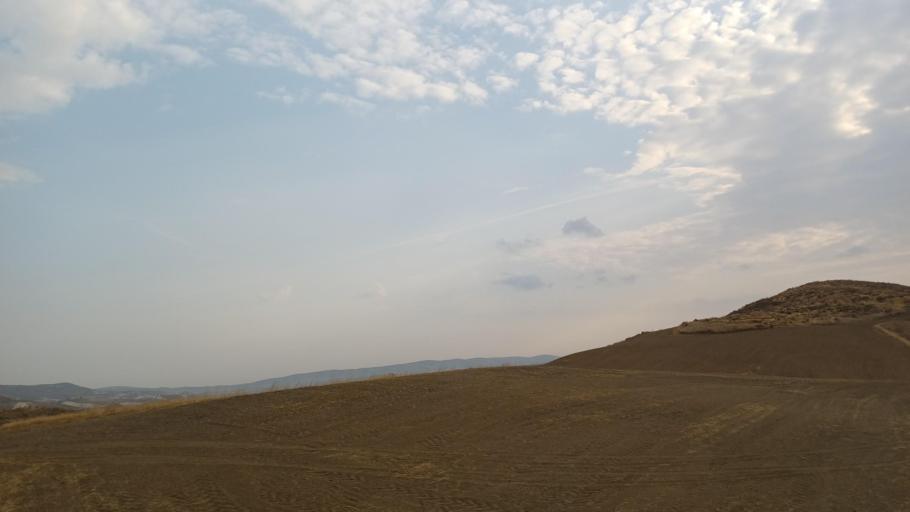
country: CY
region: Larnaka
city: Troulloi
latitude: 35.0196
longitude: 33.5742
